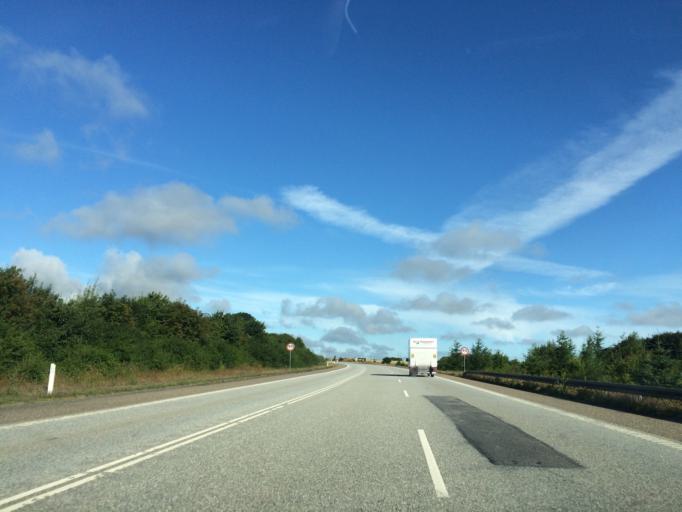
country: DK
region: Central Jutland
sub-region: Silkeborg Kommune
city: Kjellerup
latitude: 56.3544
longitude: 9.5263
